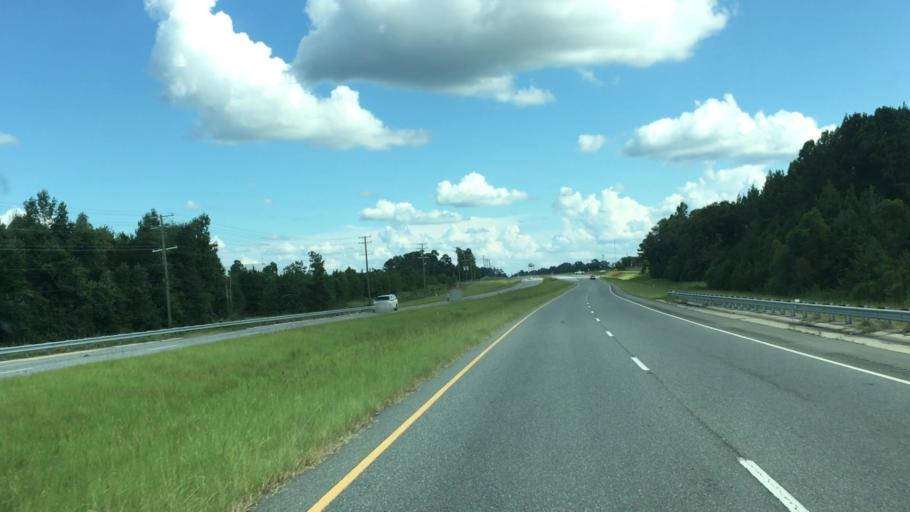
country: US
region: Georgia
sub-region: Laurens County
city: Dublin
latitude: 32.5136
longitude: -82.9537
